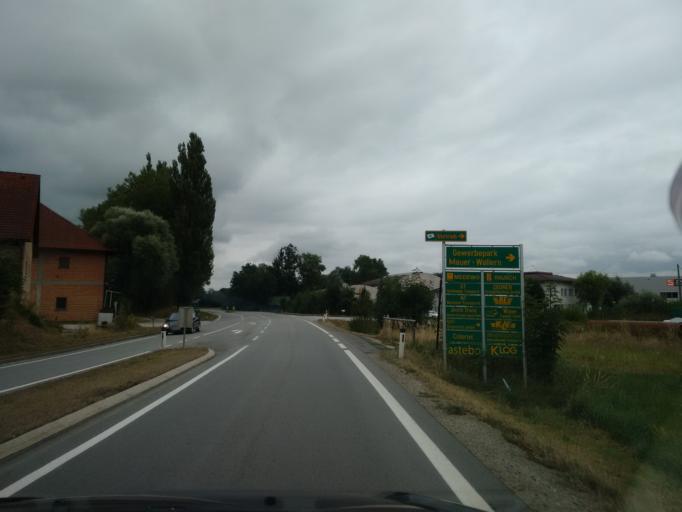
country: AT
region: Upper Austria
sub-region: Politischer Bezirk Grieskirchen
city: Bad Schallerbach
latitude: 48.2210
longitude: 13.9455
